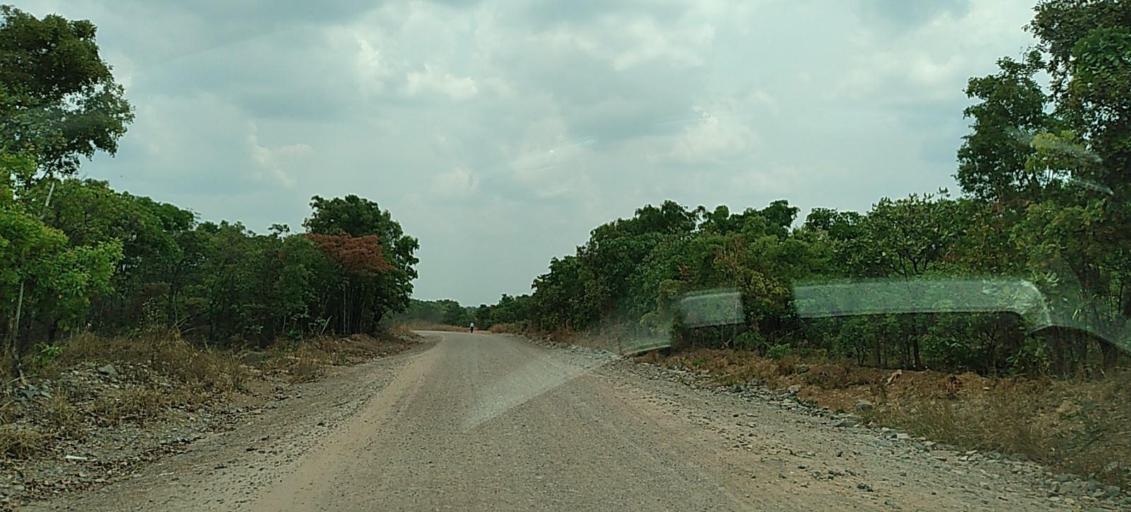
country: ZM
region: Copperbelt
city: Chililabombwe
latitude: -12.3092
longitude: 27.7910
